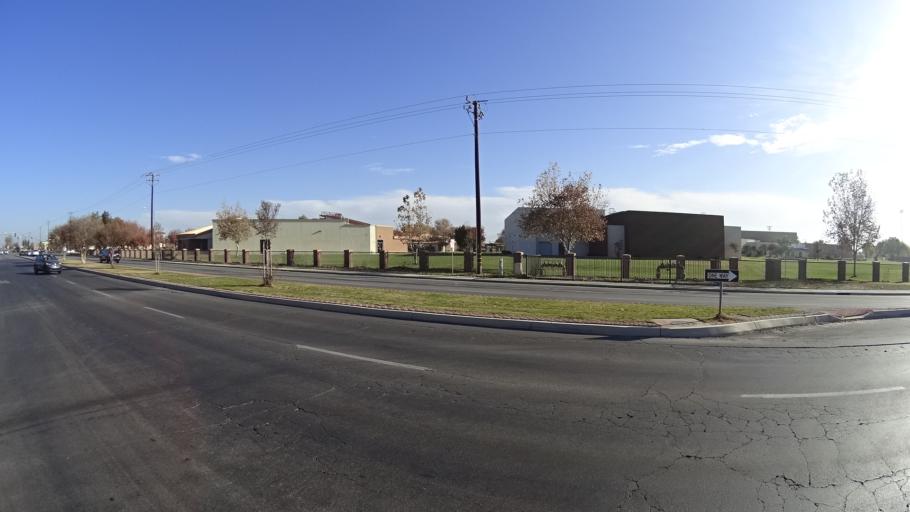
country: US
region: California
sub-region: Kern County
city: Rosedale
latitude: 35.3526
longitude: -119.1457
